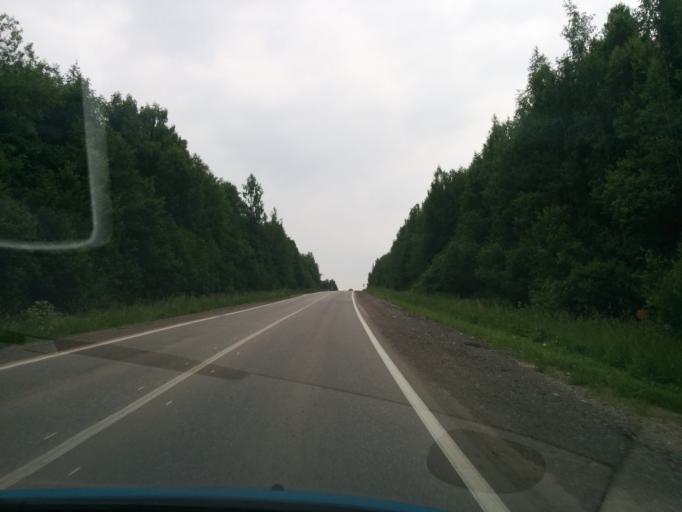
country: RU
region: Perm
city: Perm
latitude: 58.1419
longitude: 56.2669
